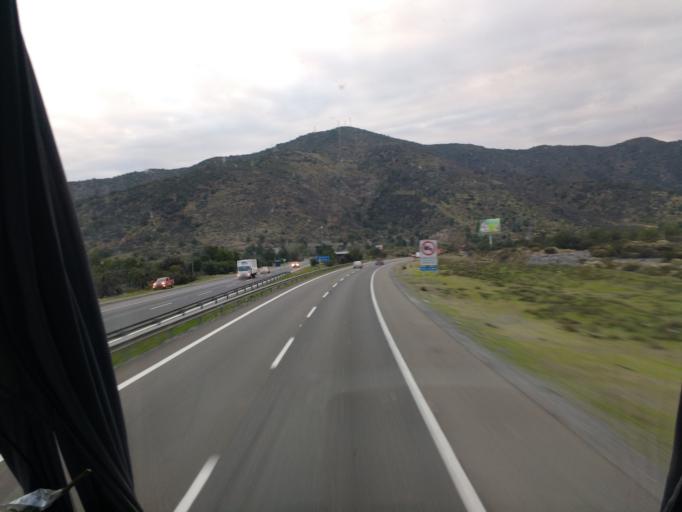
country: CL
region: Santiago Metropolitan
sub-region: Provincia de Talagante
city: Penaflor
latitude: -33.4577
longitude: -70.9254
